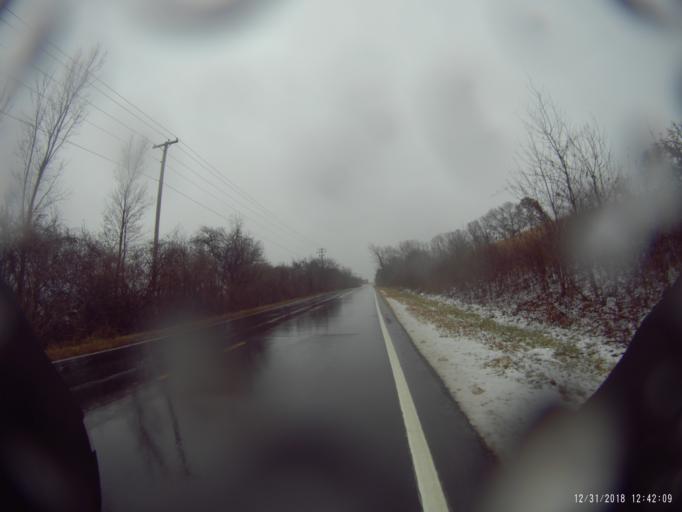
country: US
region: Wisconsin
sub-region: Dane County
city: Verona
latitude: 43.0286
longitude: -89.5124
